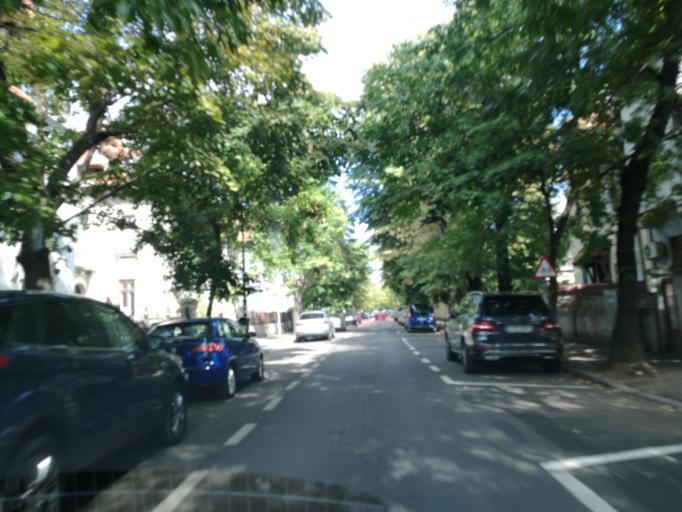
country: RO
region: Bucuresti
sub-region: Municipiul Bucuresti
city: Bucharest
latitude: 44.4572
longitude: 26.0941
